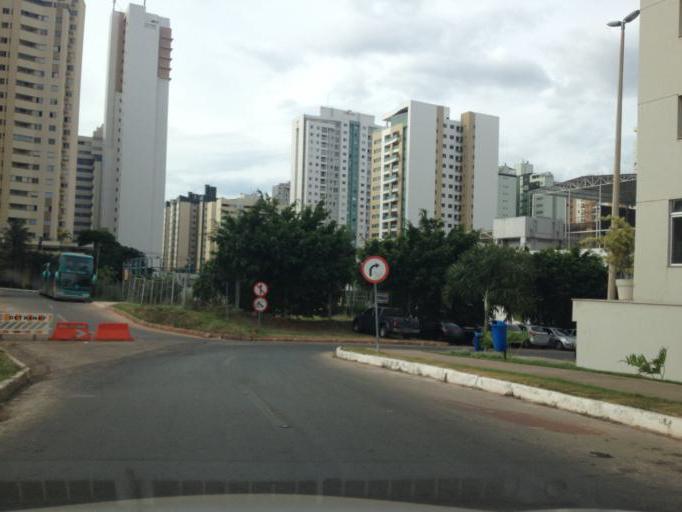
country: BR
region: Federal District
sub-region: Brasilia
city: Brasilia
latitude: -15.8394
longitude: -48.0308
